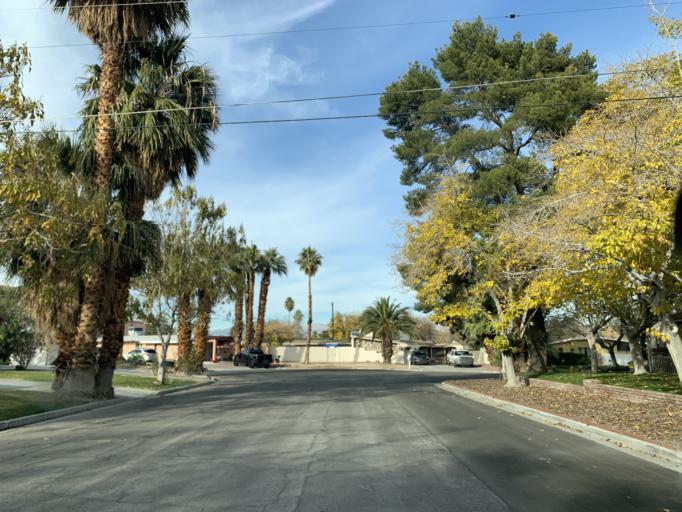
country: US
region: Nevada
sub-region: Clark County
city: Las Vegas
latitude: 36.1494
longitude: -115.1714
